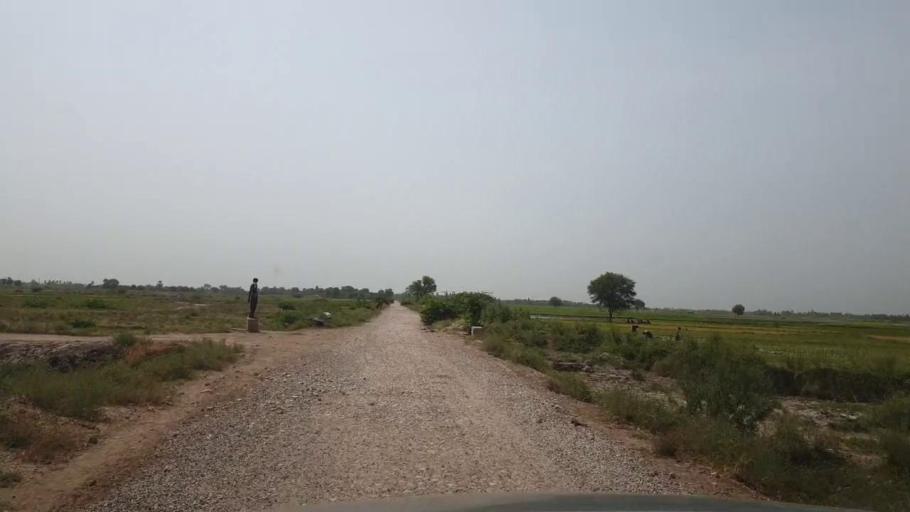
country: PK
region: Sindh
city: Madeji
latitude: 27.8336
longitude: 68.4270
